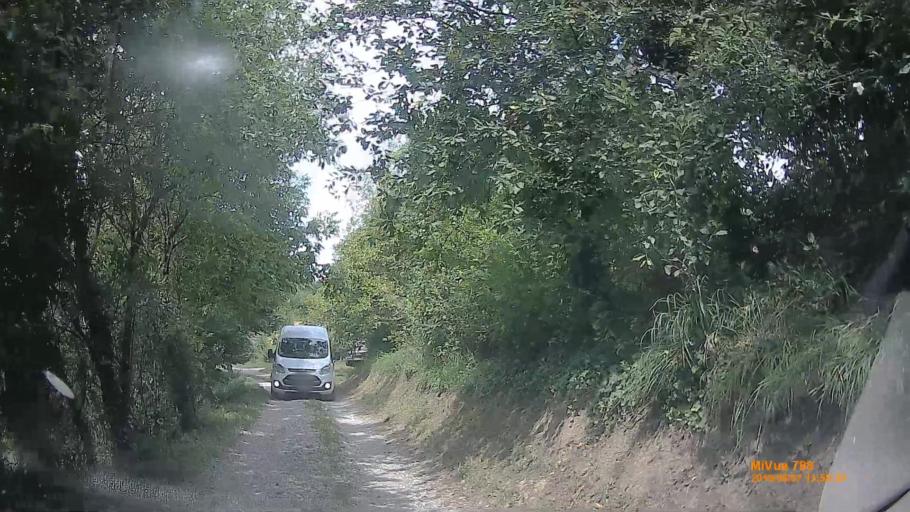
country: HU
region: Zala
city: Cserszegtomaj
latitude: 46.8966
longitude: 17.1768
